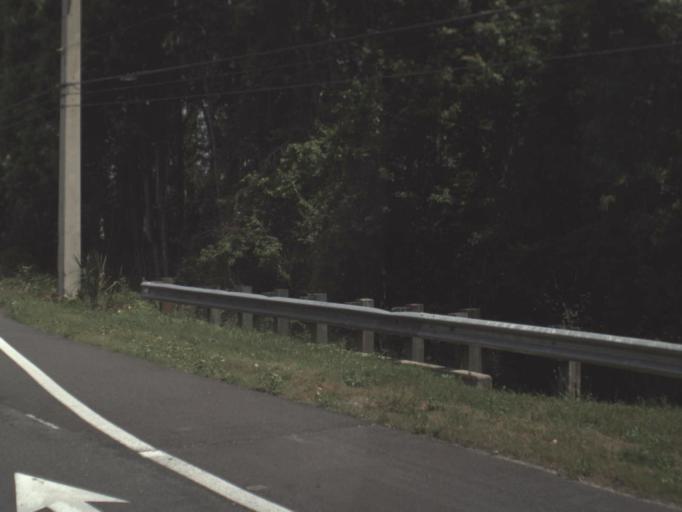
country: US
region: Florida
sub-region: Saint Johns County
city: Fruit Cove
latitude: 30.1984
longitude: -81.5713
